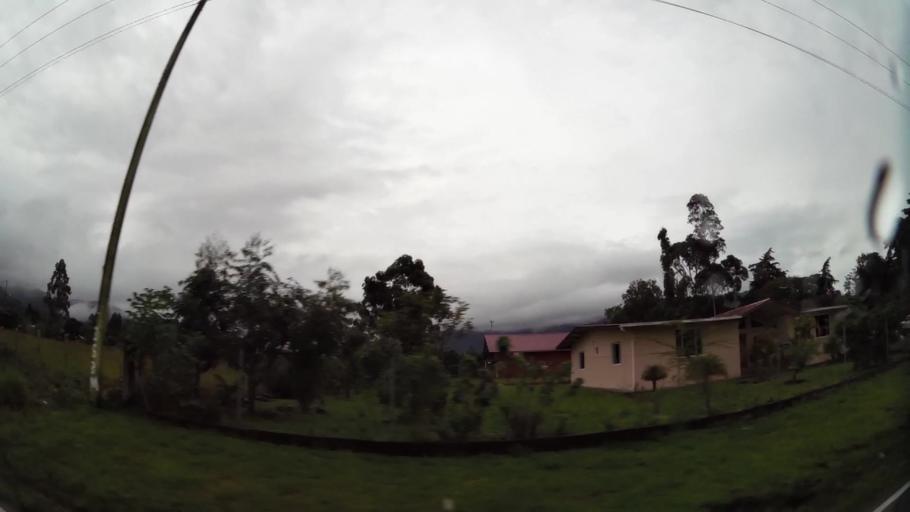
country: PA
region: Chiriqui
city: Volcan
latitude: 8.7776
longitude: -82.6384
